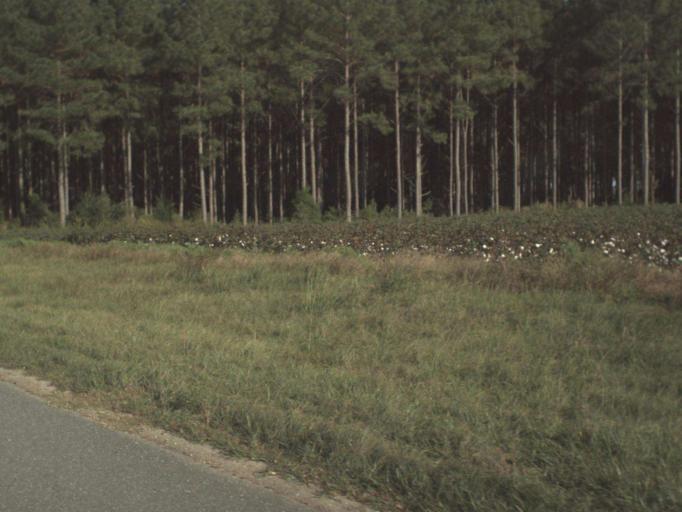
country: US
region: Florida
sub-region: Holmes County
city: Bonifay
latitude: 30.6509
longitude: -85.6745
